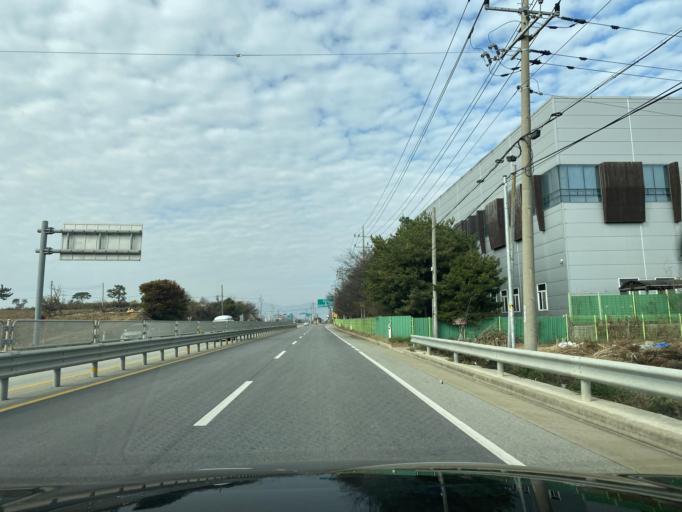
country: KR
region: Chungcheongnam-do
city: Yesan
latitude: 36.6889
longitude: 126.7537
